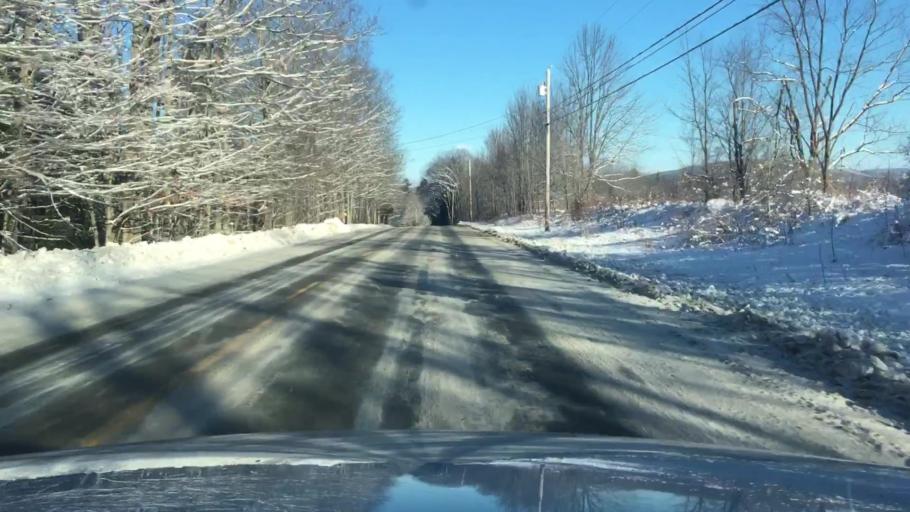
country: US
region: Maine
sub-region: Kennebec County
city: Mount Vernon
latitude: 44.4649
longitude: -69.9734
